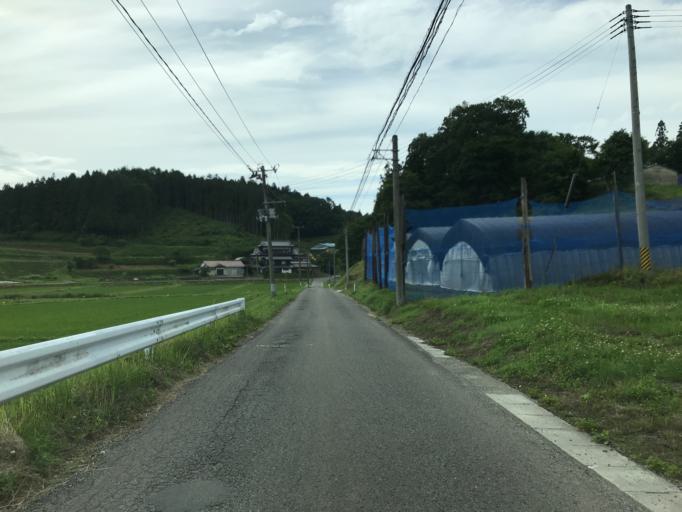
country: JP
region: Fukushima
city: Funehikimachi-funehiki
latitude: 37.4998
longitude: 140.6519
